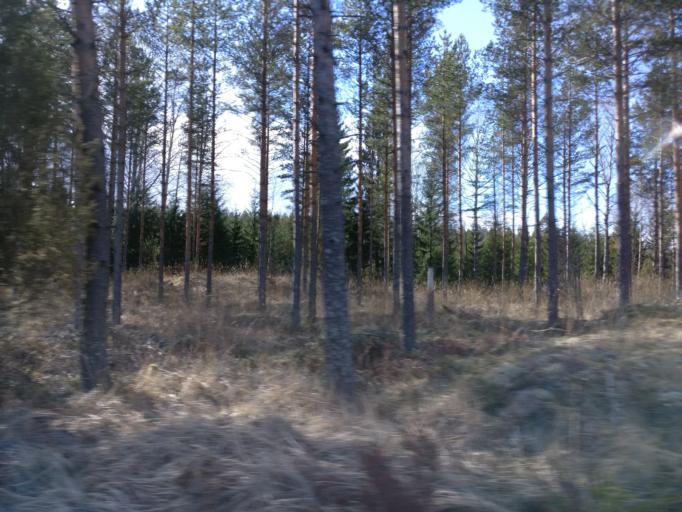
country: FI
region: Varsinais-Suomi
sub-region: Salo
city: Suomusjaervi
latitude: 60.3271
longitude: 23.6485
